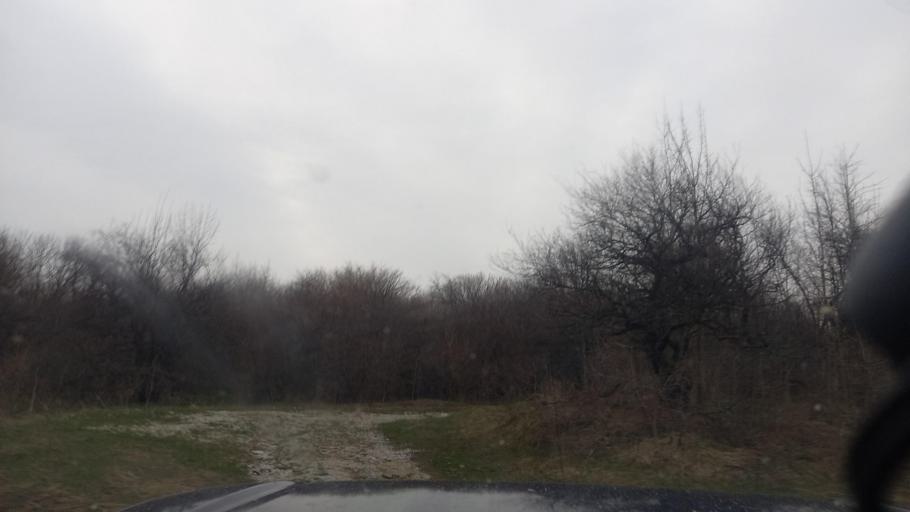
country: RU
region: Krasnodarskiy
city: Pshada
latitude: 44.5981
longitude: 38.2814
